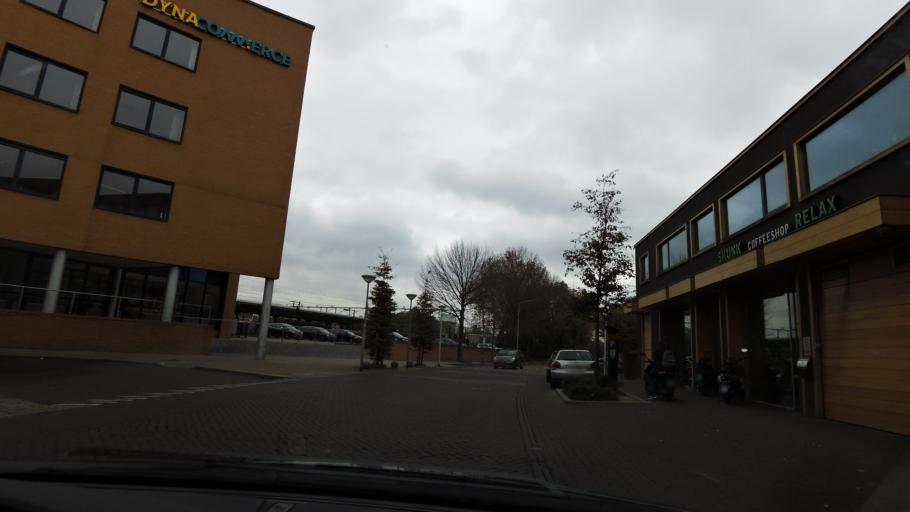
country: NL
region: Limburg
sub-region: Gemeente Sittard-Geleen
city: Sittard
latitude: 51.0020
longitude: 5.8597
